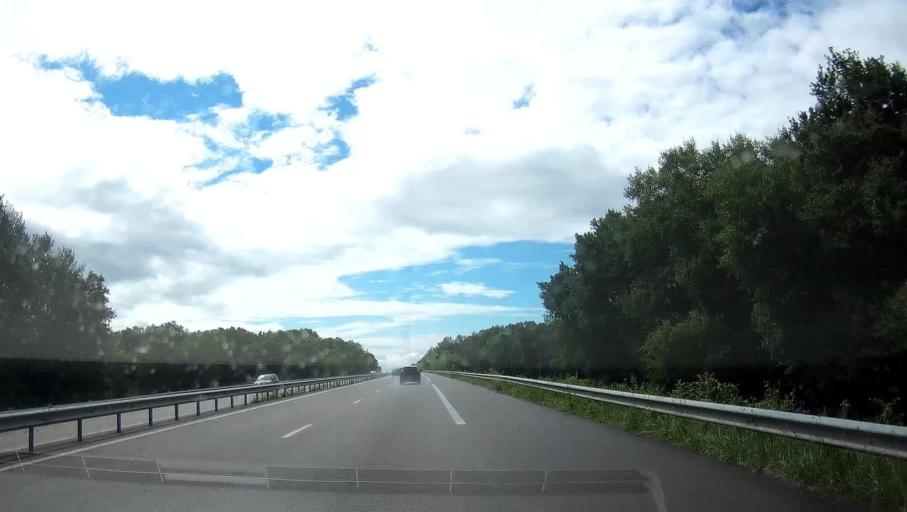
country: FR
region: Champagne-Ardenne
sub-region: Departement de l'Aube
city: Verrieres
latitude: 48.2652
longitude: 4.1645
